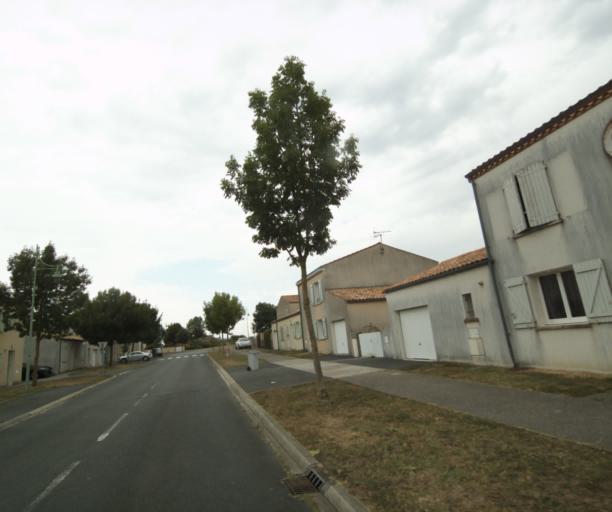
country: FR
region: Poitou-Charentes
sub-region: Departement de la Charente-Maritime
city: Tonnay-Charente
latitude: 45.9488
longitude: -0.8959
